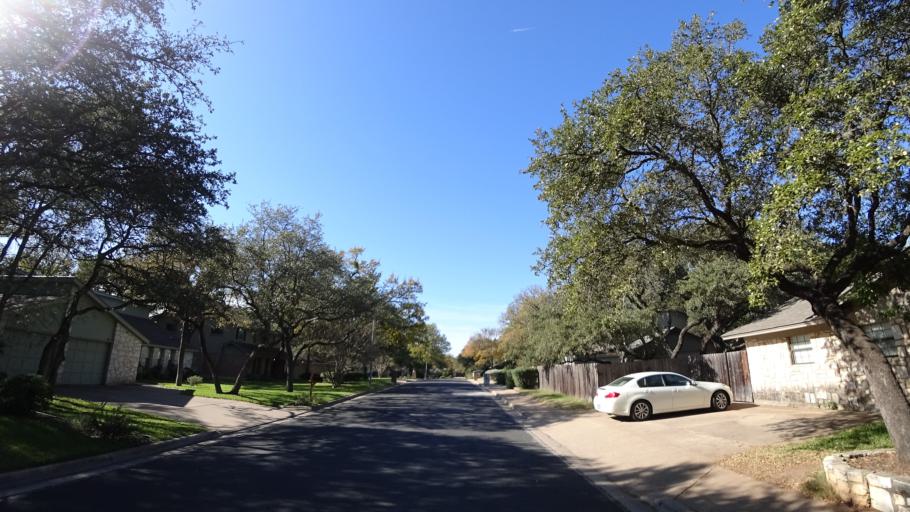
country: US
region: Texas
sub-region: Williamson County
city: Jollyville
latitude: 30.4205
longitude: -97.7708
